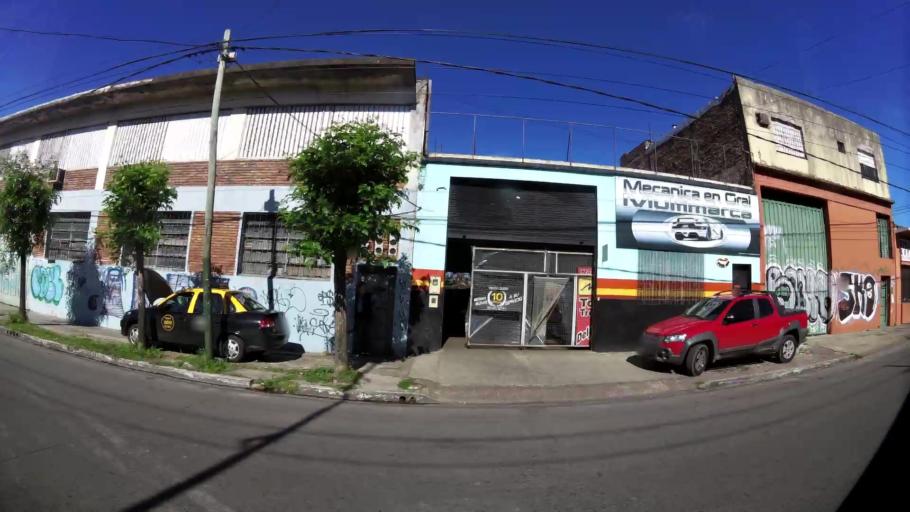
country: AR
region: Buenos Aires
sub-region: Partido de Lomas de Zamora
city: Lomas de Zamora
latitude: -34.7683
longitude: -58.4231
